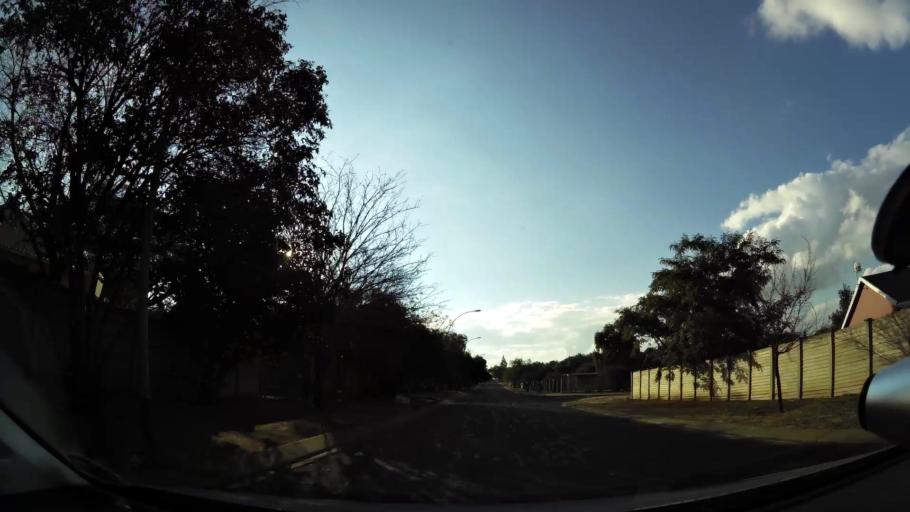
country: ZA
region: Orange Free State
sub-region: Mangaung Metropolitan Municipality
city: Bloemfontein
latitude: -29.1593
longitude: 26.1790
